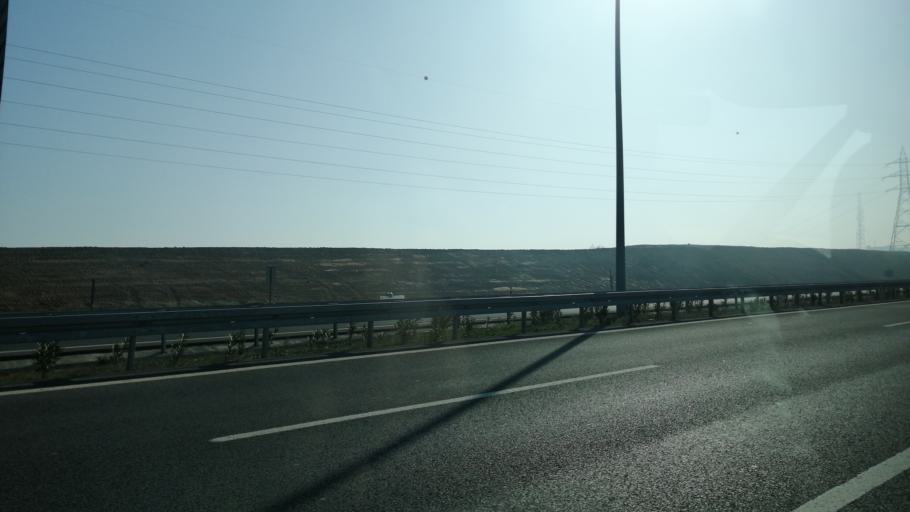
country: TR
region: Kocaeli
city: Tavsanli
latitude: 40.7897
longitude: 29.5141
